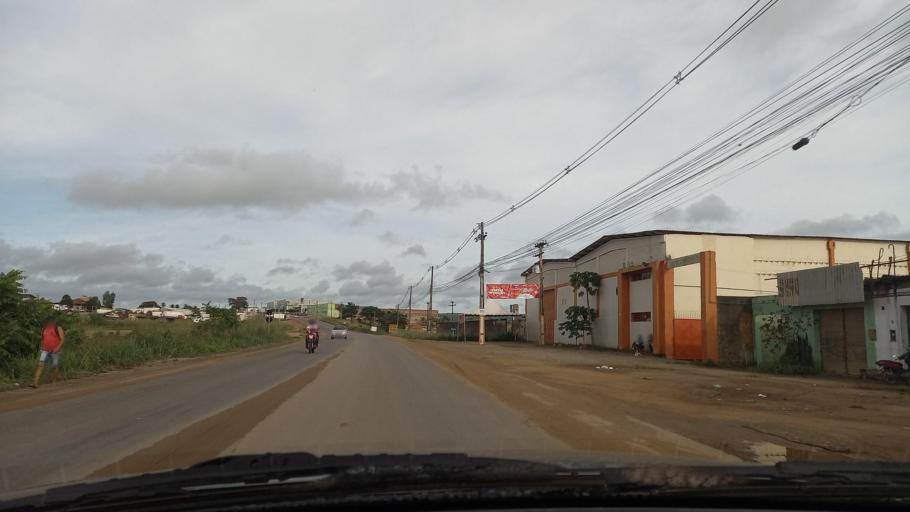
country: BR
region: Pernambuco
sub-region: Vitoria De Santo Antao
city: Vitoria de Santo Antao
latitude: -8.1213
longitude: -35.3278
